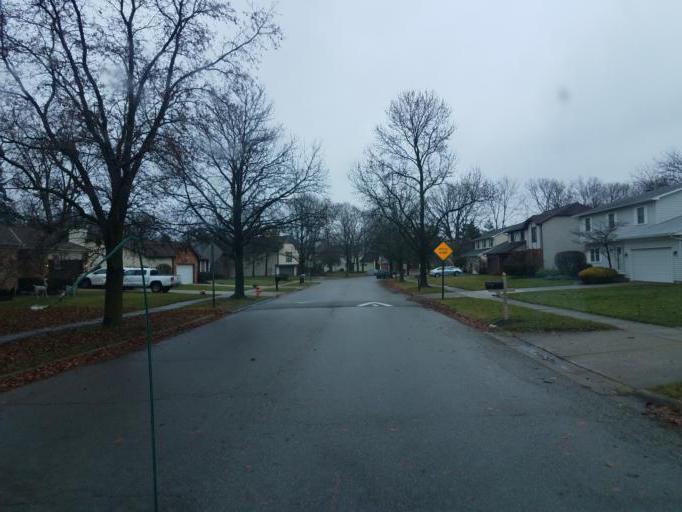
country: US
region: Ohio
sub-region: Franklin County
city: Dublin
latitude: 40.0697
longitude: -83.0704
